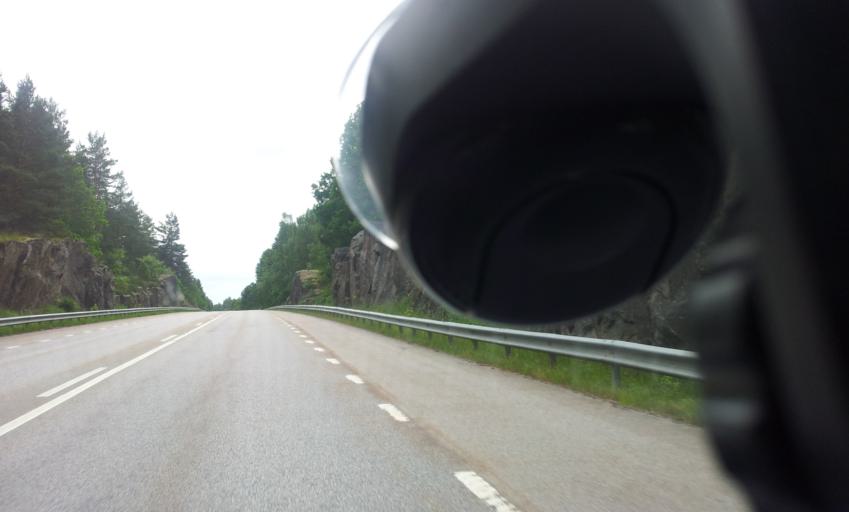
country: SE
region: Kalmar
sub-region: Vasterviks Kommun
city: Ankarsrum
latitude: 57.7073
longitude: 16.4465
